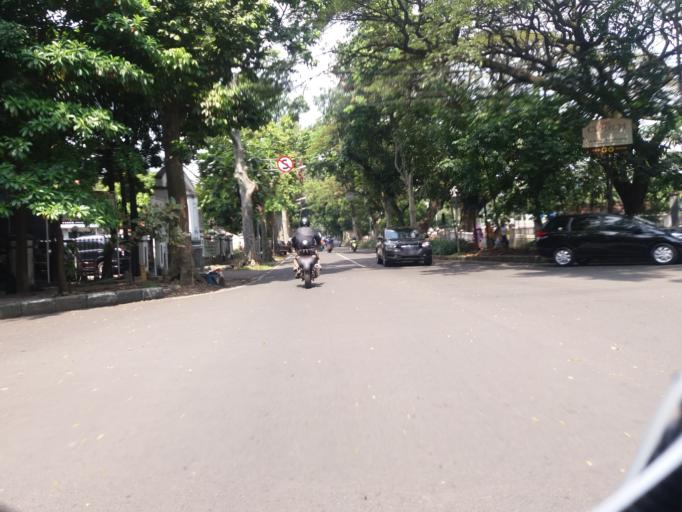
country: ID
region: West Java
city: Bandung
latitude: -6.9074
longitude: 107.6171
